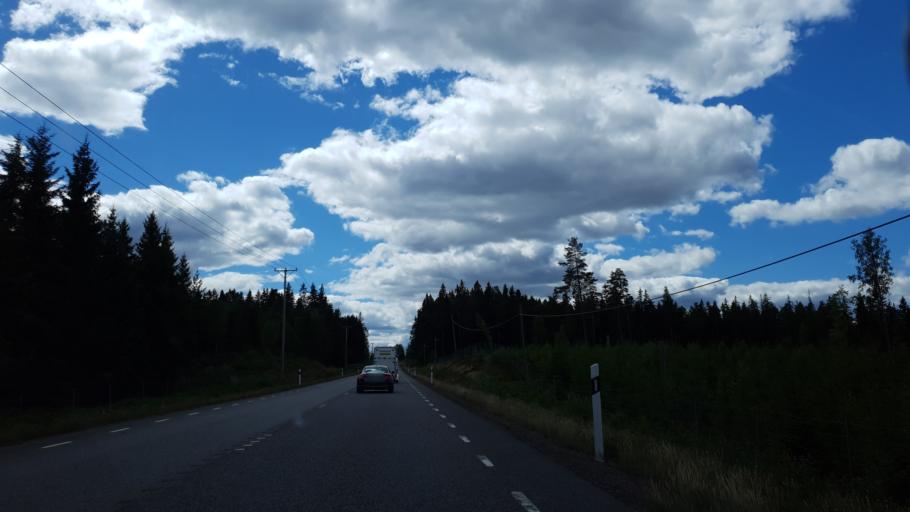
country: SE
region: Kronoberg
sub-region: Vaxjo Kommun
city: Braas
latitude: 57.1719
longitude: 15.1613
